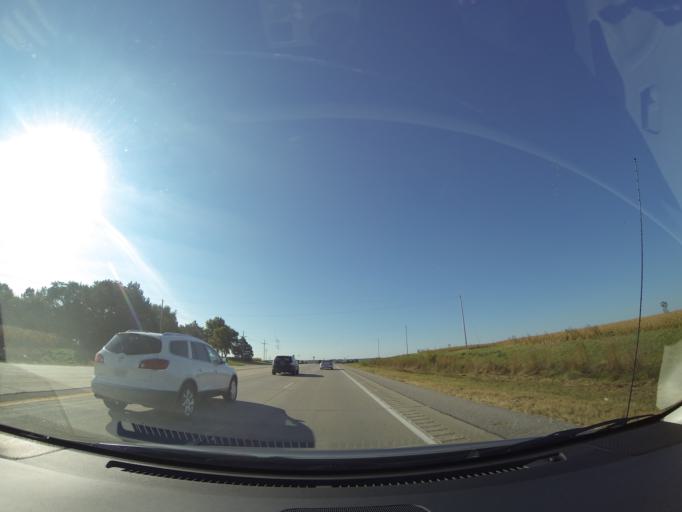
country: US
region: Nebraska
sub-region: Sarpy County
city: Gretna
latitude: 41.1877
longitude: -96.2343
